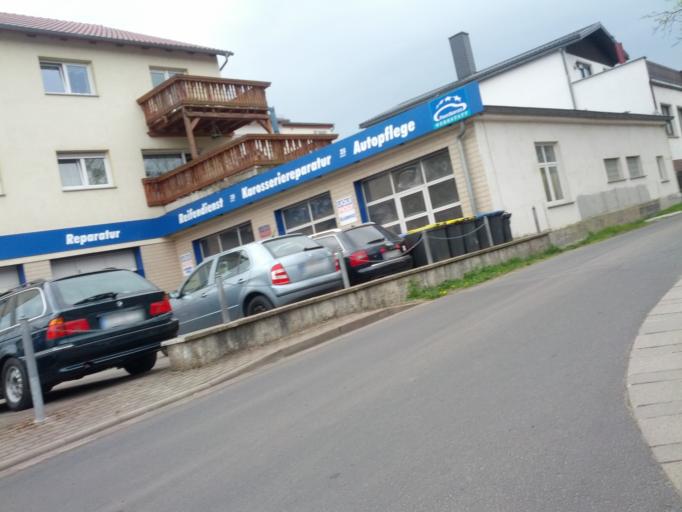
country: DE
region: Thuringia
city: Thal
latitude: 50.9572
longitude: 10.3954
